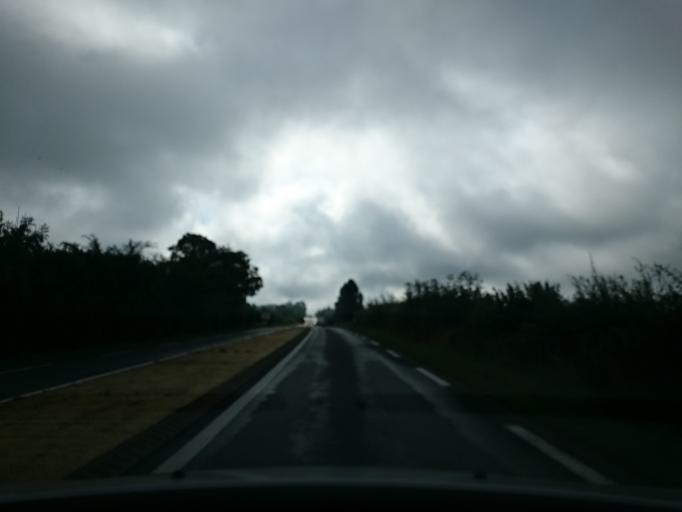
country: FR
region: Lower Normandy
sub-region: Departement du Calvados
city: Saint-Desir
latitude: 49.1355
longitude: 0.1351
